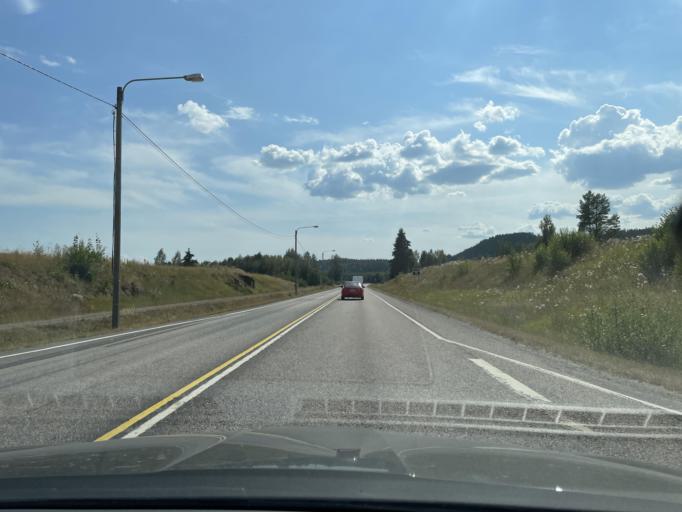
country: FI
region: Central Finland
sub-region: Jaemsae
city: Jaemsae
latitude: 61.9345
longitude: 25.3484
